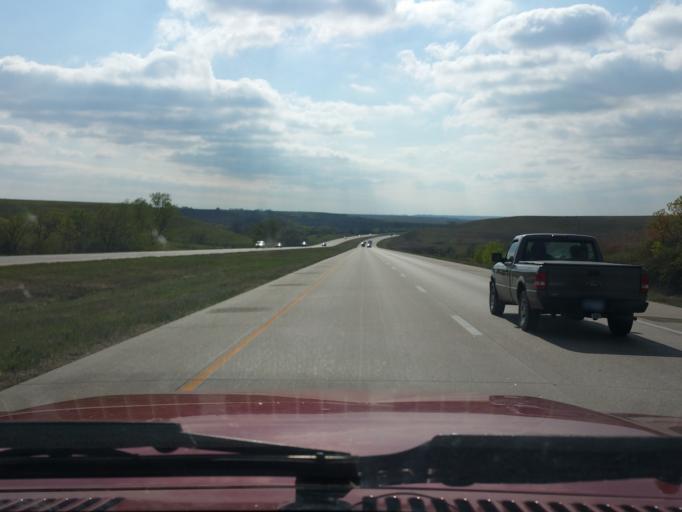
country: US
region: Kansas
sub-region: Wabaunsee County
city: Alma
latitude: 39.0648
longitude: -96.4360
